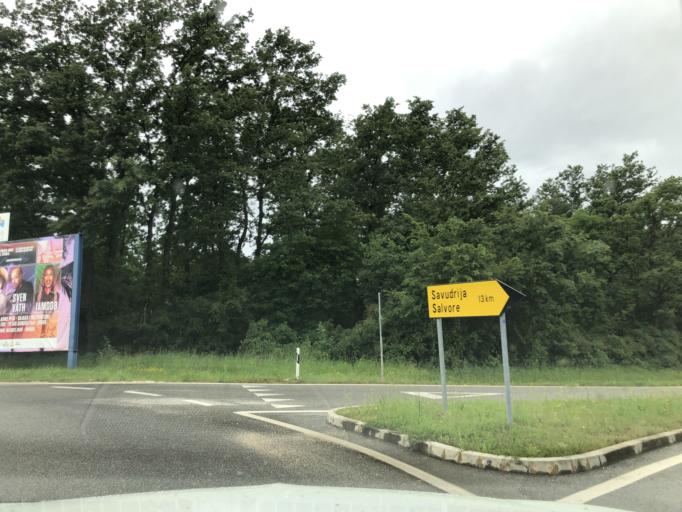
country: SI
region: Piran-Pirano
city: Seca
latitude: 45.4599
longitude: 13.6015
